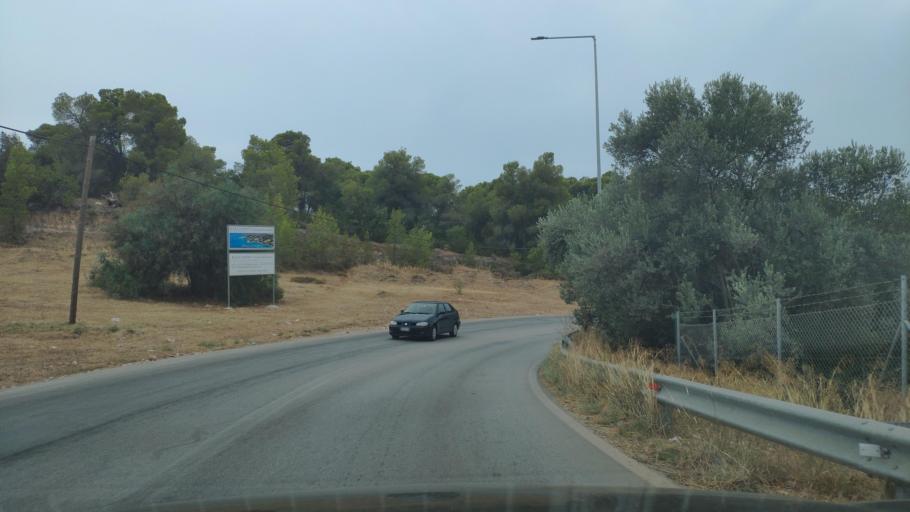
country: GR
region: Peloponnese
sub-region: Nomos Argolidos
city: Porto Cheli
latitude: 37.3339
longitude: 23.1522
